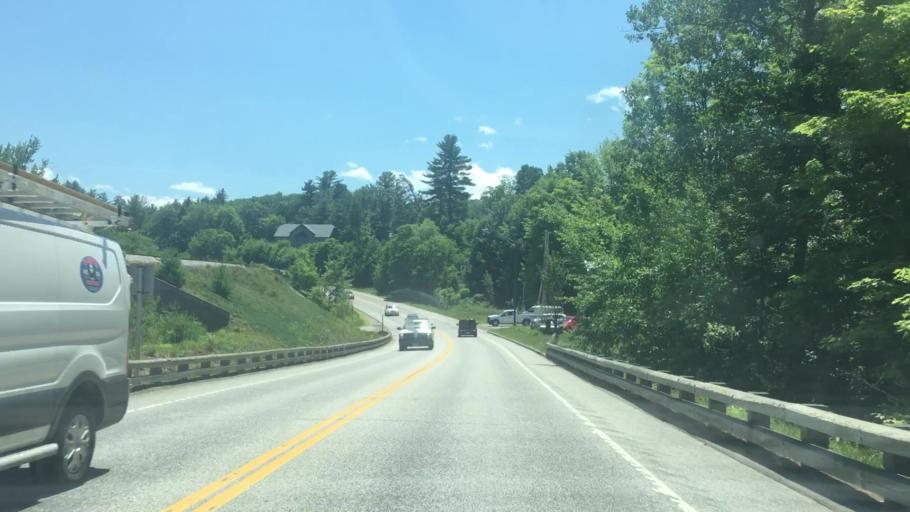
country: US
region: New Hampshire
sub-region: Carroll County
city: North Conway
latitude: 44.0457
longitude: -71.1225
